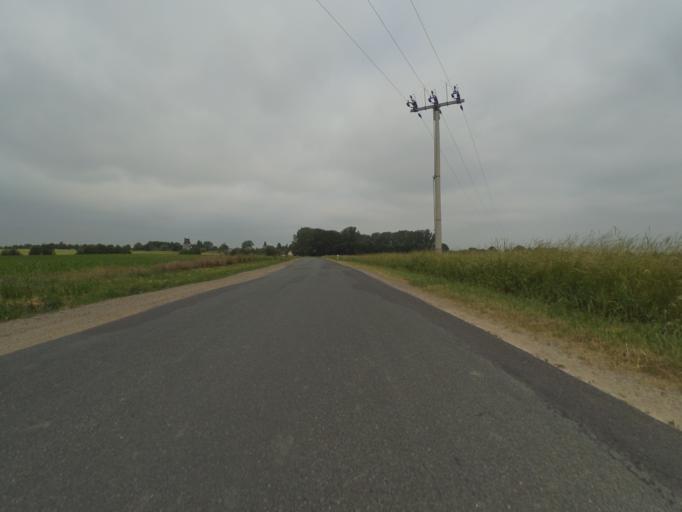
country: DE
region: Mecklenburg-Vorpommern
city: Goldberg
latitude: 53.5082
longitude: 12.1309
